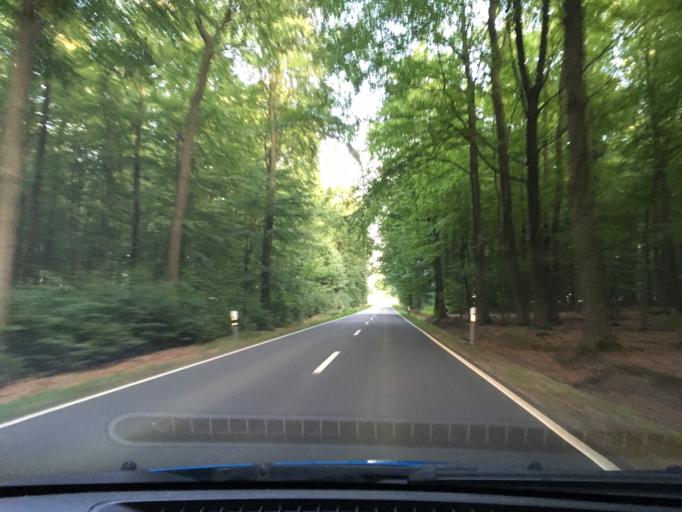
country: DE
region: Lower Saxony
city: Tosterglope
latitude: 53.2246
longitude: 10.8074
